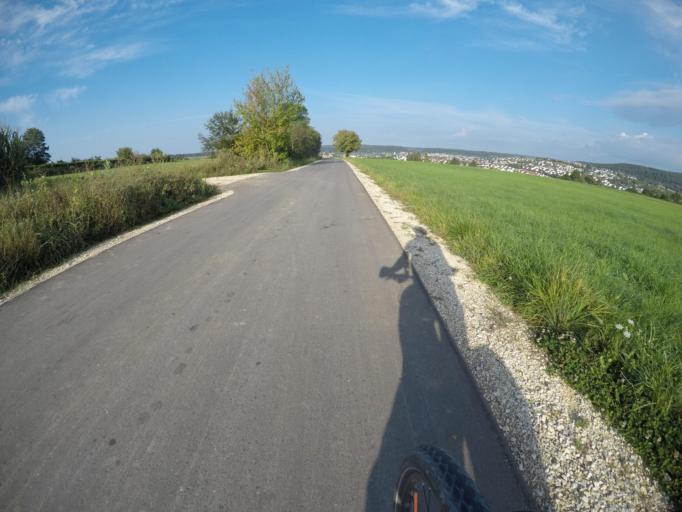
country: DE
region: Baden-Wuerttemberg
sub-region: Regierungsbezirk Stuttgart
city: Herbrechtingen
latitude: 48.6218
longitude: 10.1926
